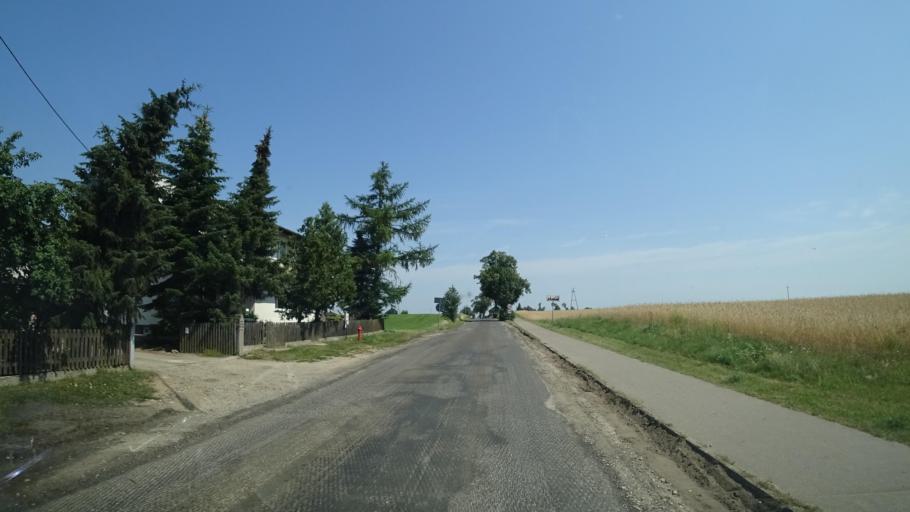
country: PL
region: Pomeranian Voivodeship
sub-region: Powiat chojnicki
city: Brusy
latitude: 53.8751
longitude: 17.6850
